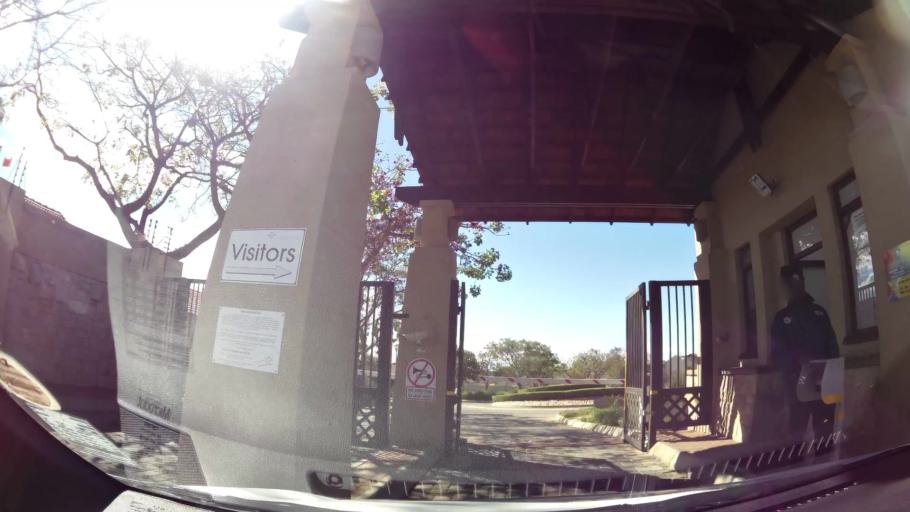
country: ZA
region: Limpopo
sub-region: Capricorn District Municipality
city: Polokwane
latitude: -23.8856
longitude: 29.5040
